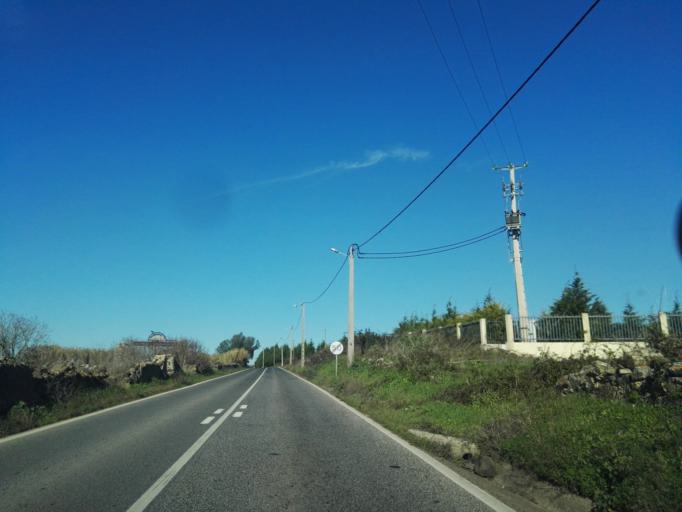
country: PT
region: Lisbon
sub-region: Loures
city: Loures
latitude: 38.8781
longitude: -9.1849
